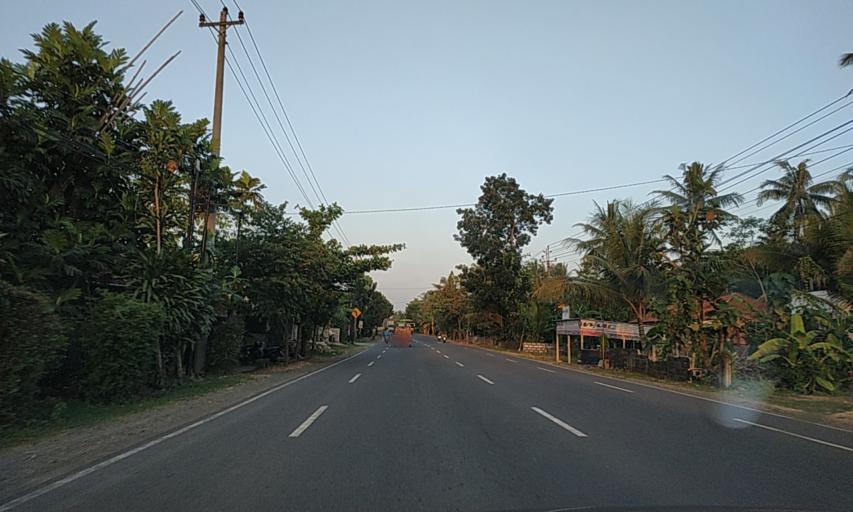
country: ID
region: Daerah Istimewa Yogyakarta
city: Srandakan
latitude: -7.8899
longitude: 110.1040
